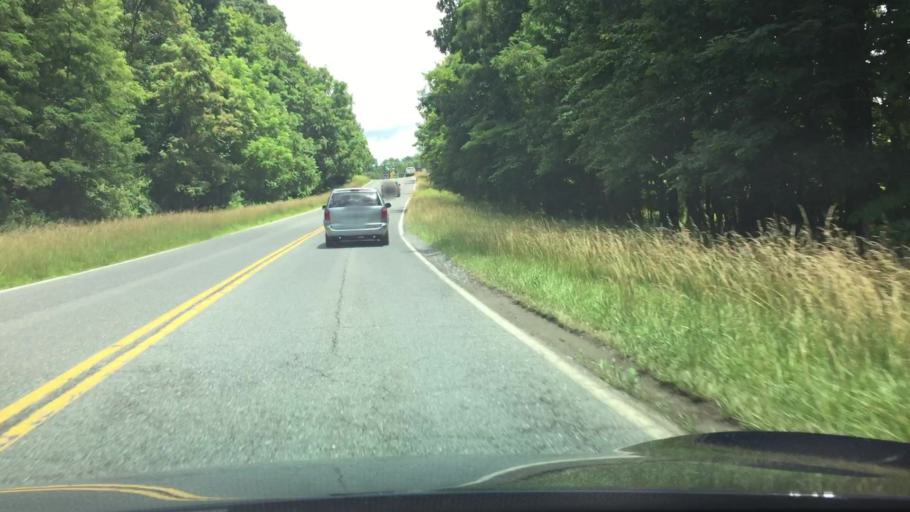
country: US
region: Virginia
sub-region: Bedford County
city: Forest
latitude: 37.3668
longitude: -79.2551
